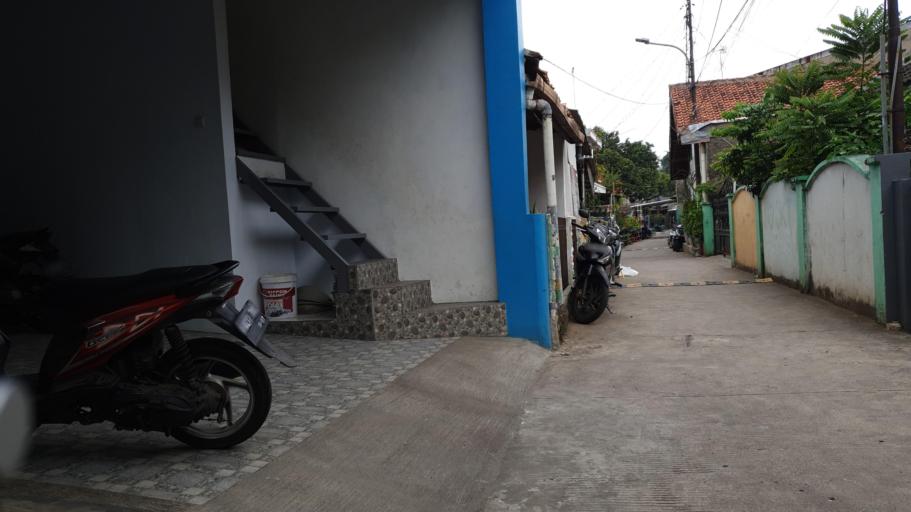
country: ID
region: Banten
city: South Tangerang
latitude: -6.2888
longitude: 106.7921
